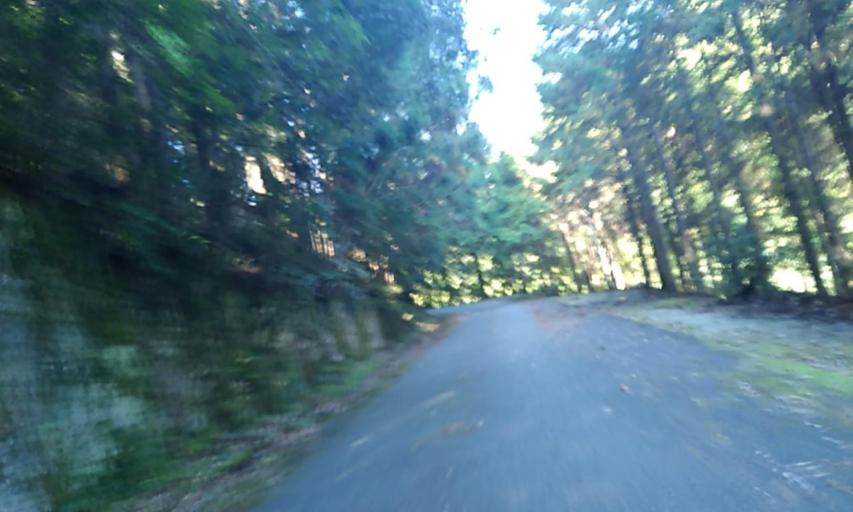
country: JP
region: Wakayama
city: Shingu
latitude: 33.9096
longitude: 135.9913
